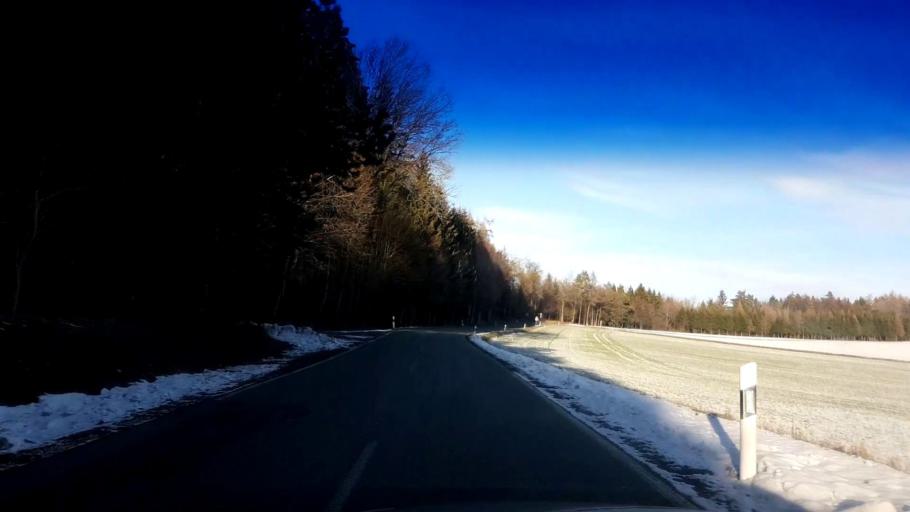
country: DE
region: Bavaria
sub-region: Upper Franconia
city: Heiligenstadt
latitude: 49.8548
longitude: 11.1493
